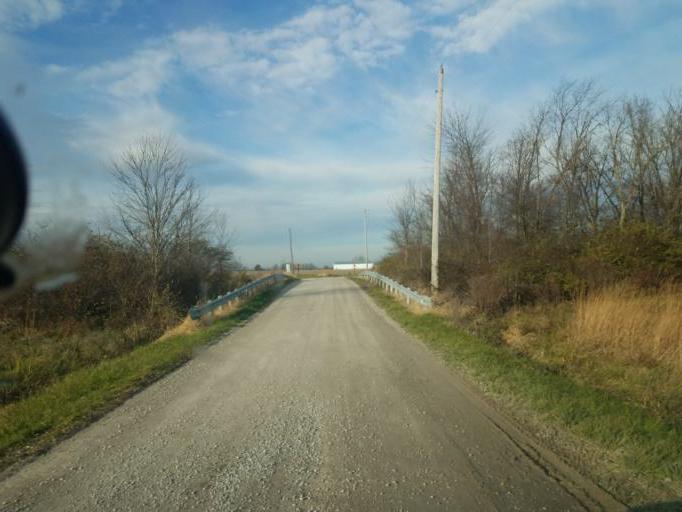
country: US
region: Ohio
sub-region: Morrow County
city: Mount Gilead
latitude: 40.5783
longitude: -82.8704
